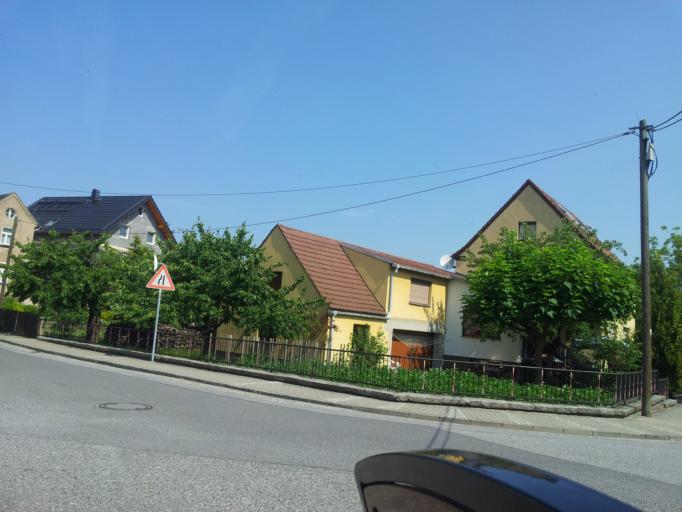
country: DE
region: Saxony
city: Panschwitz-Kuckau
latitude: 51.2320
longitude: 14.1986
